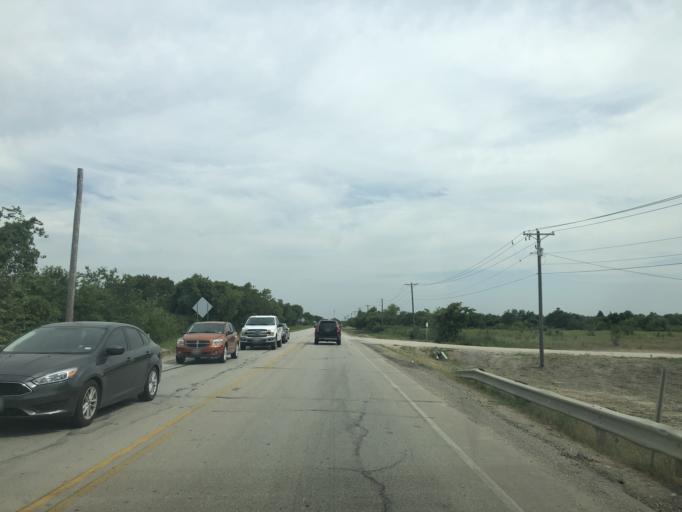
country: US
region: Texas
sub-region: Tarrant County
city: Saginaw
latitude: 32.8939
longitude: -97.3485
